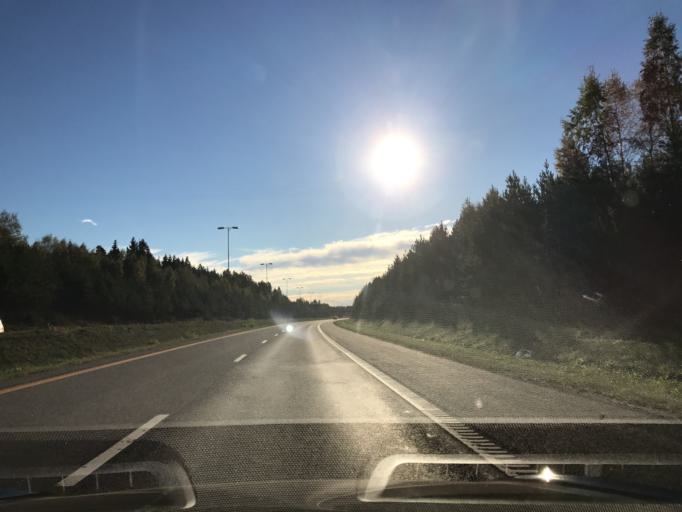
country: NO
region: Akershus
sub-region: Ullensaker
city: Jessheim
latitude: 60.1657
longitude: 11.1304
